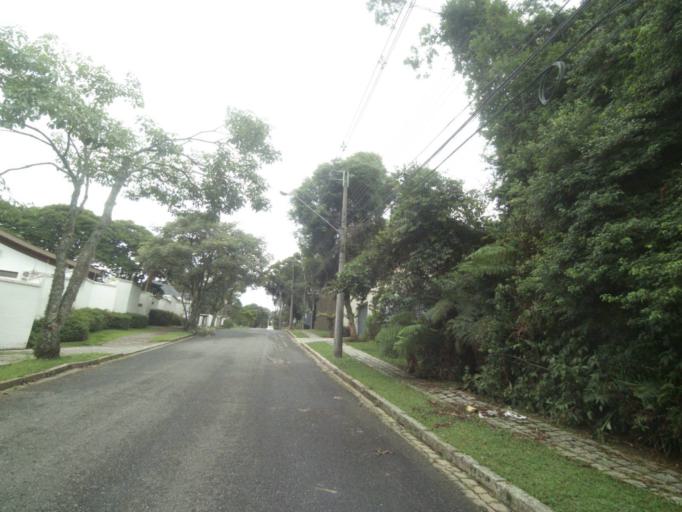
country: BR
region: Parana
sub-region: Curitiba
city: Curitiba
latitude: -25.4032
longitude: -49.2850
